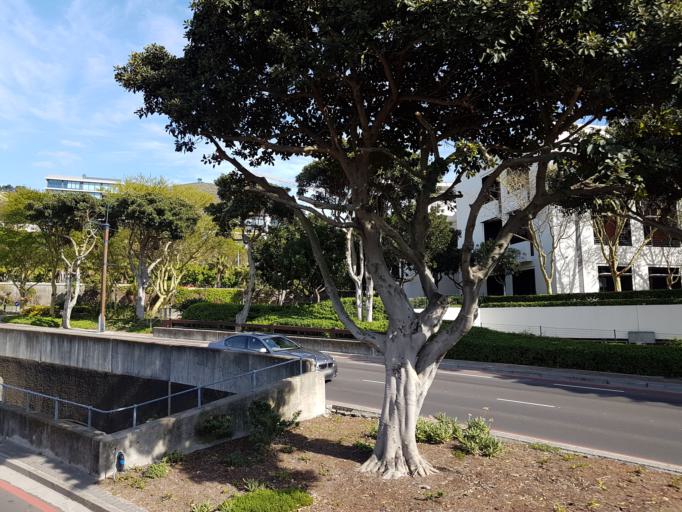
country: ZA
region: Western Cape
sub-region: City of Cape Town
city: Cape Town
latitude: -33.9092
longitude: 18.4152
